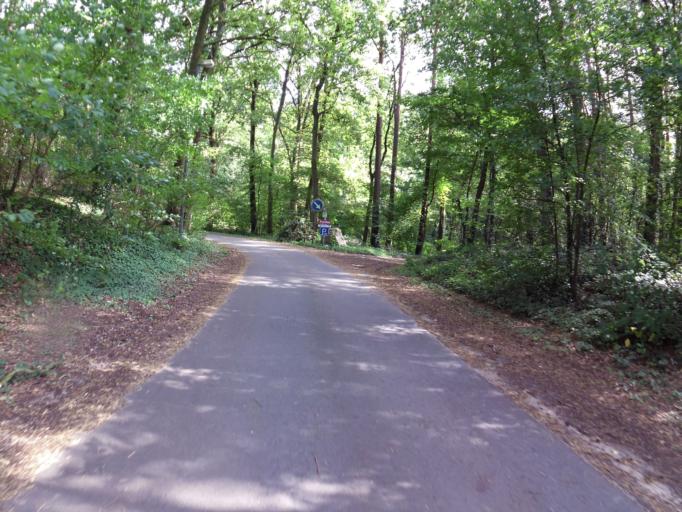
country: DE
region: Lower Saxony
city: Heeslingen
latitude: 53.2958
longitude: 9.3772
